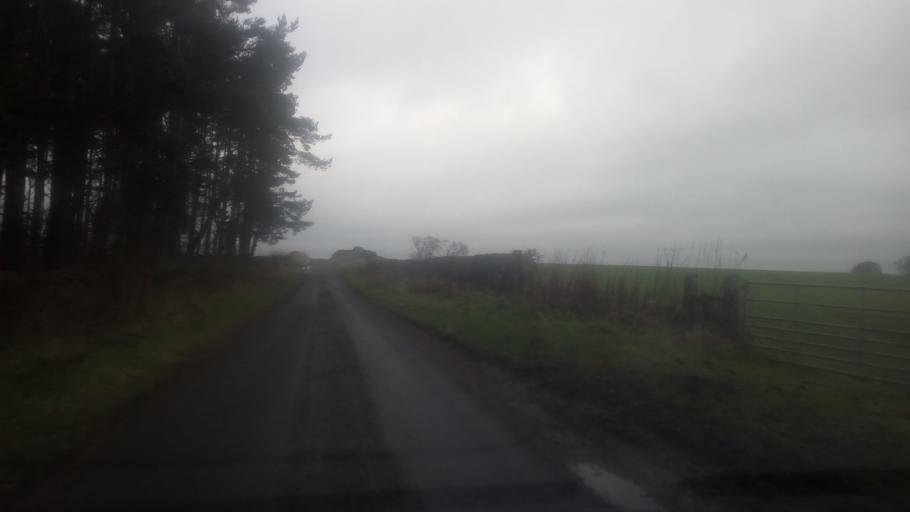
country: GB
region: Scotland
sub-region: The Scottish Borders
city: Kelso
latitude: 55.5653
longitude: -2.5068
